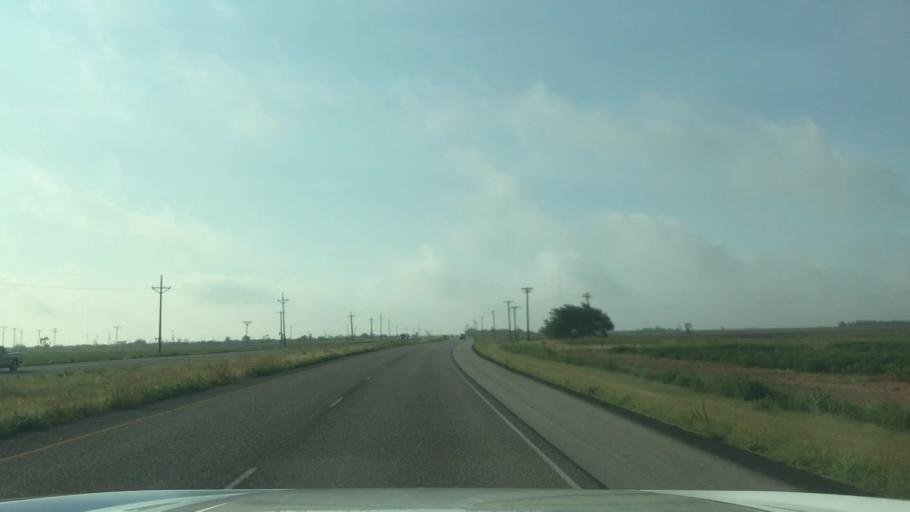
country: US
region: Texas
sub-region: Garza County
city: Post
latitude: 33.2422
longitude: -101.4563
